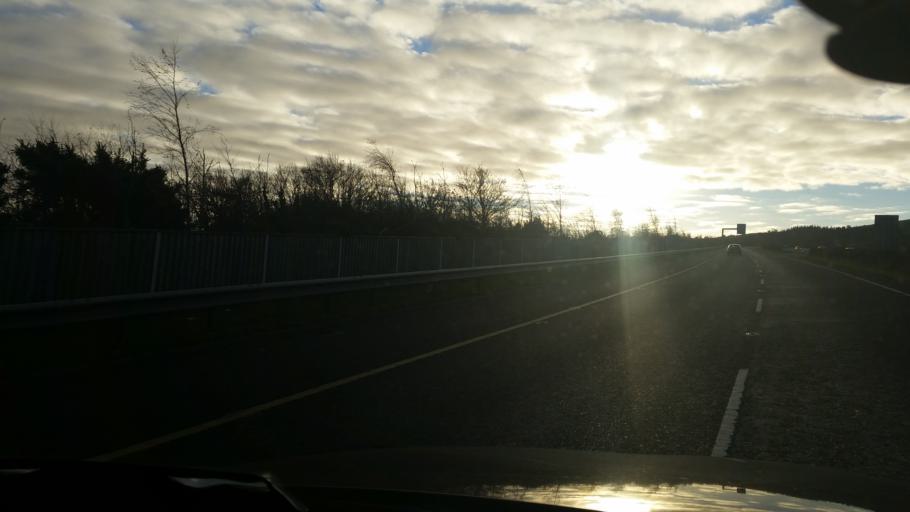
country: IE
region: Leinster
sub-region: Wicklow
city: Rathnew
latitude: 52.9903
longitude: -6.0943
